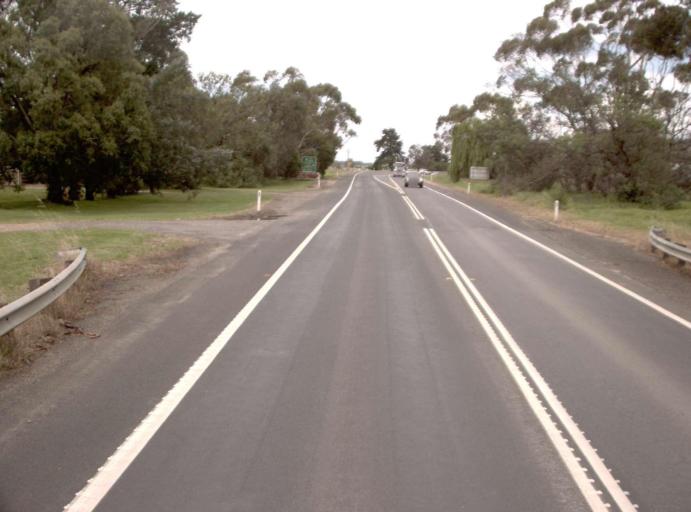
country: AU
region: Victoria
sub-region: Wellington
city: Sale
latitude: -37.9792
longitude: 147.0726
